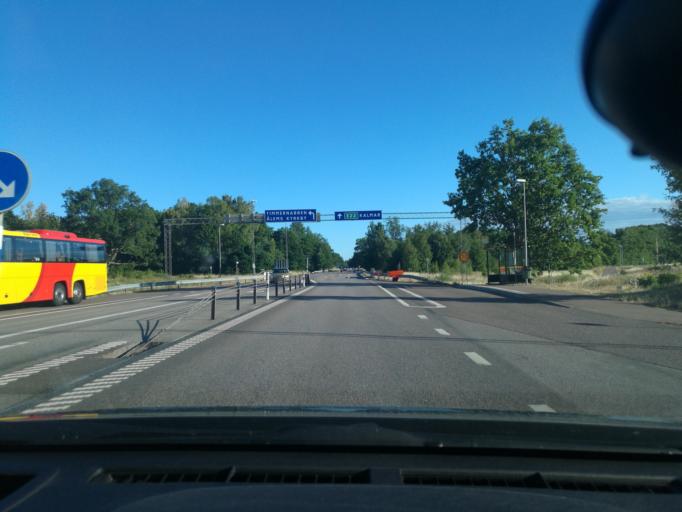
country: SE
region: Kalmar
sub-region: Monsteras Kommun
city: Timmernabben
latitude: 56.9583
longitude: 16.3906
